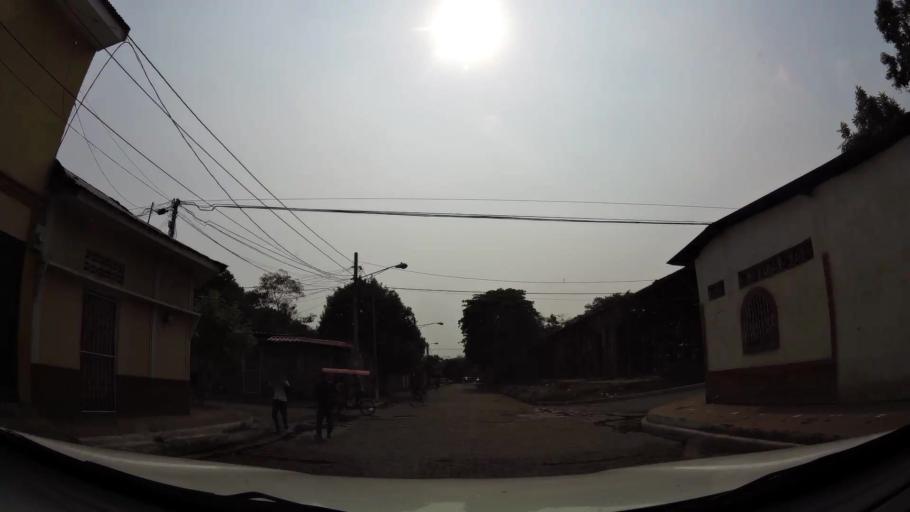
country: NI
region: Chinandega
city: Chinandega
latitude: 12.6226
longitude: -87.1316
